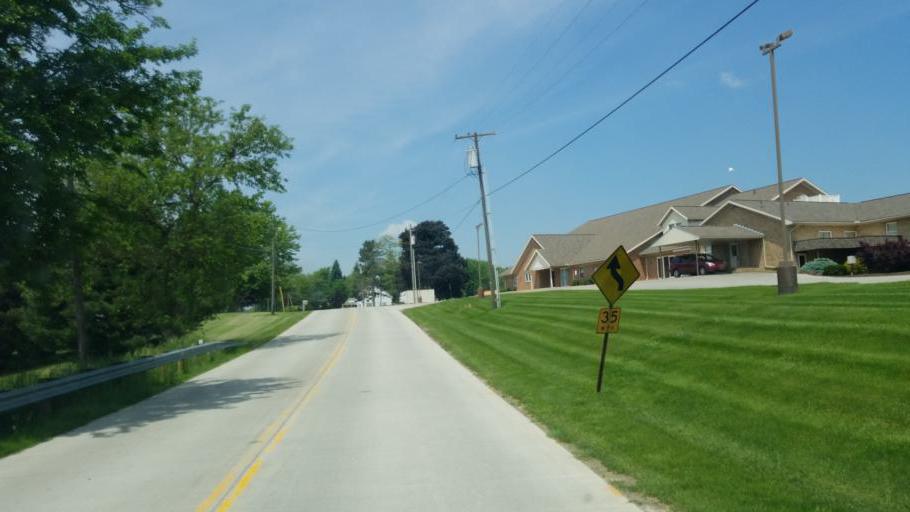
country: US
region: Ohio
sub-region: Tuscarawas County
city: Sugarcreek
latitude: 40.5183
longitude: -81.6840
